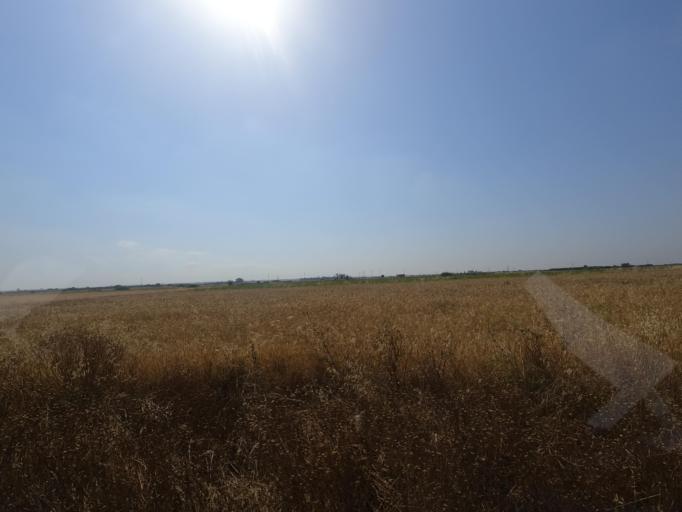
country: CY
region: Ammochostos
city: Avgorou
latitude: 35.0593
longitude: 33.8585
